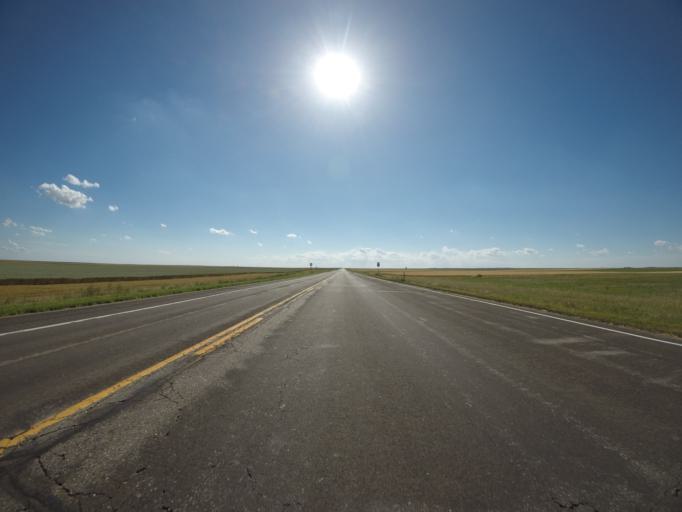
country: US
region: Colorado
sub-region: Logan County
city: Sterling
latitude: 40.6240
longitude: -103.3579
